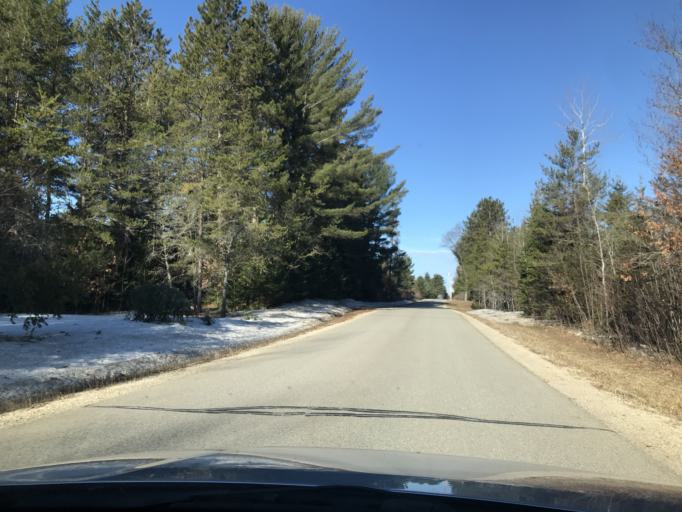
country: US
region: Wisconsin
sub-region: Marinette County
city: Niagara
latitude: 45.3983
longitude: -88.0880
